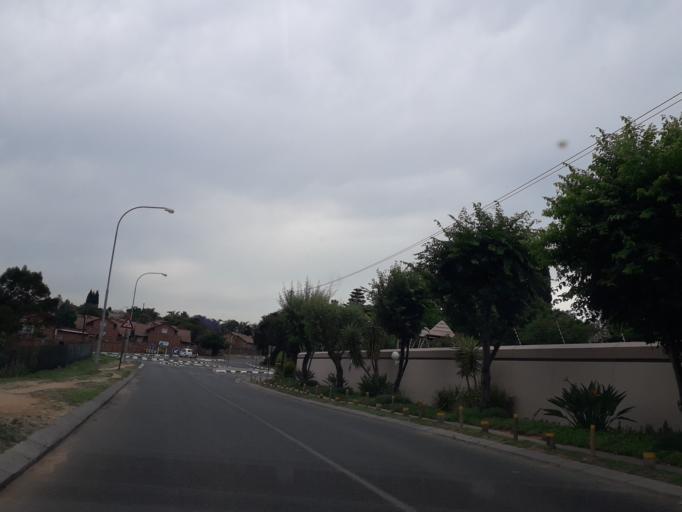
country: ZA
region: Gauteng
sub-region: City of Johannesburg Metropolitan Municipality
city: Roodepoort
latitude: -26.1112
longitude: 27.9162
